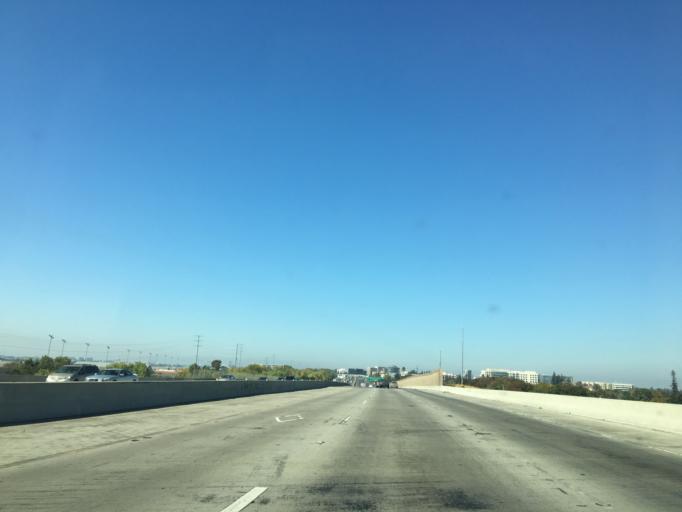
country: US
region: California
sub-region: Santa Clara County
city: San Jose
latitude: 37.3536
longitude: -121.9108
